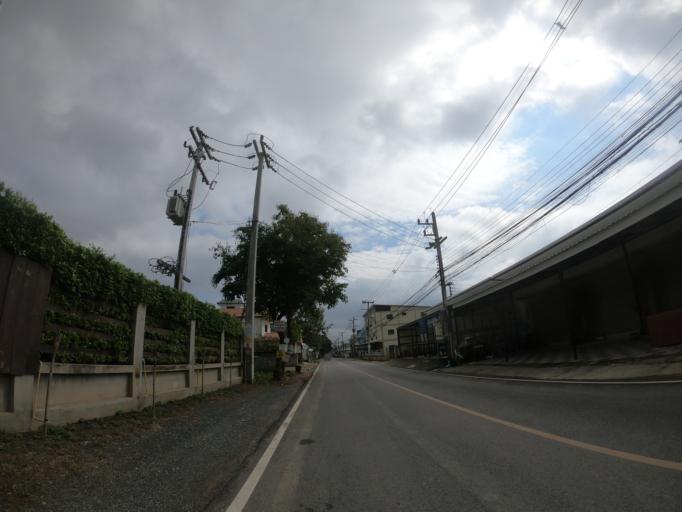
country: TH
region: Chiang Mai
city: Chiang Mai
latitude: 18.7502
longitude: 98.9765
